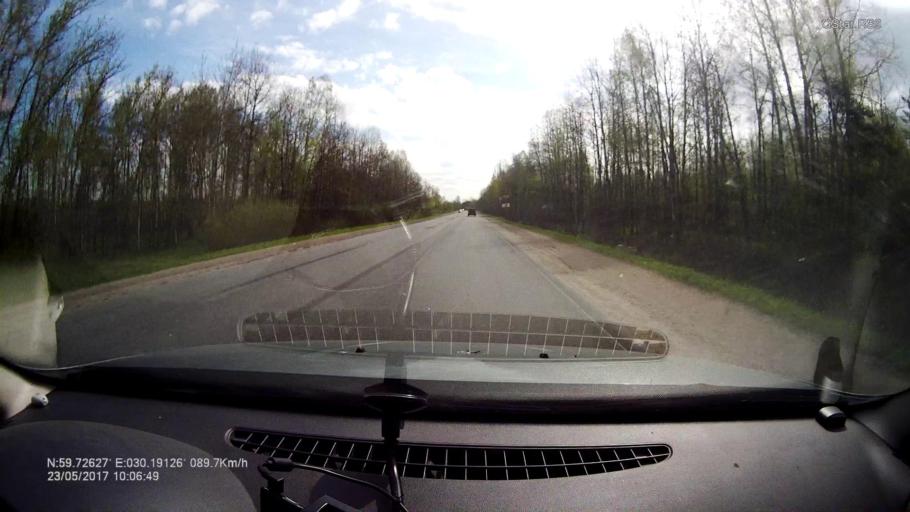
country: RU
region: St.-Petersburg
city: Gorelovo
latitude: 59.7263
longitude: 30.1922
